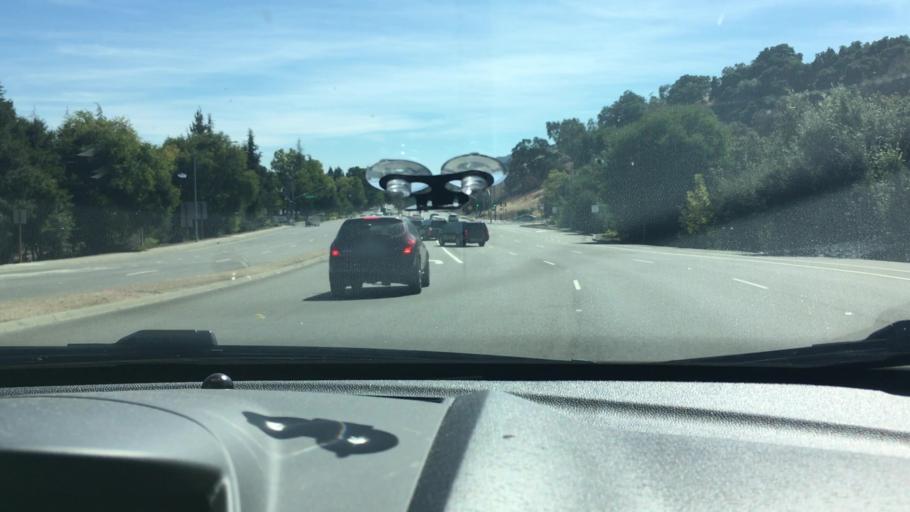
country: US
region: California
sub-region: Alameda County
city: Dublin
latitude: 37.6963
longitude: -121.9347
